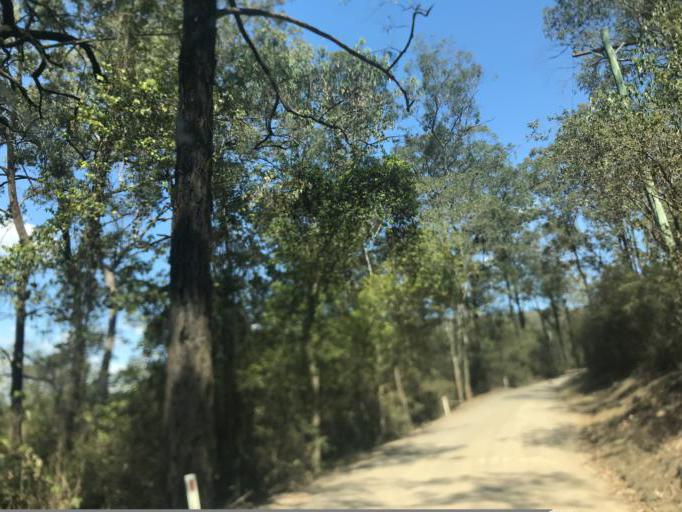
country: AU
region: New South Wales
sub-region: Hawkesbury
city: Pitt Town
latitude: -33.4154
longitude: 150.9159
